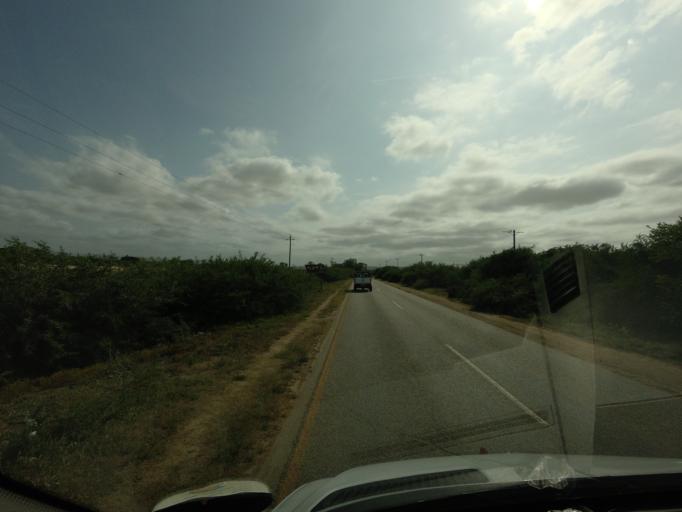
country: ZA
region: Eastern Cape
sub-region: Cacadu District Municipality
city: Kirkwood
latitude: -33.5597
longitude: 25.6855
